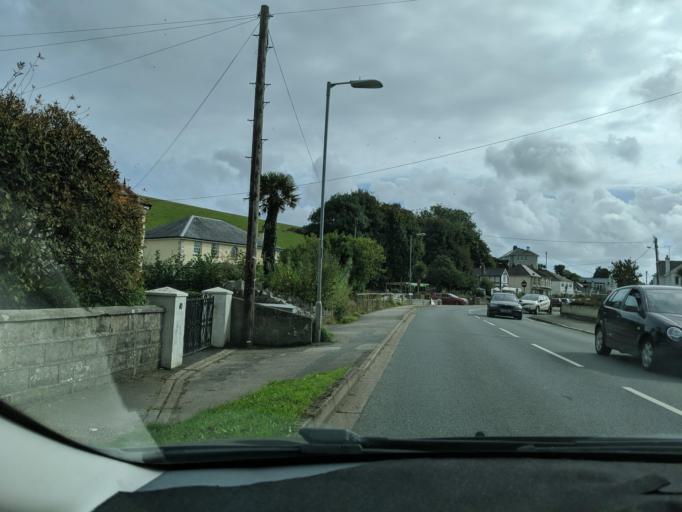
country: GB
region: England
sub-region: Cornwall
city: Par
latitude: 50.3544
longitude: -4.7007
